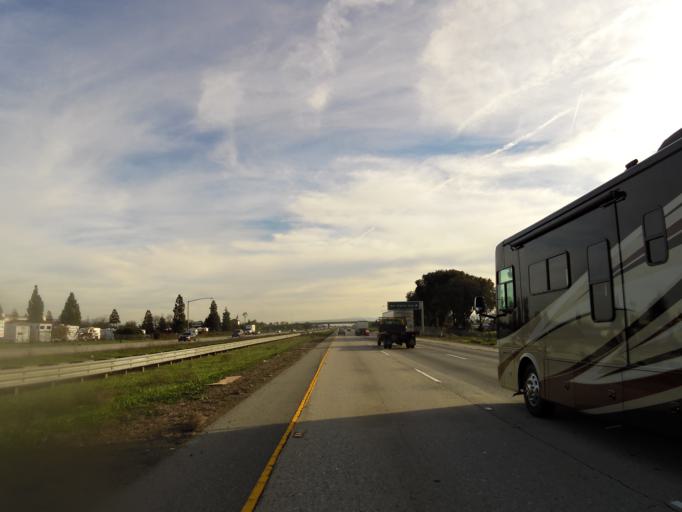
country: US
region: California
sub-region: Santa Clara County
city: San Martin
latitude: 37.0934
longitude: -121.6021
